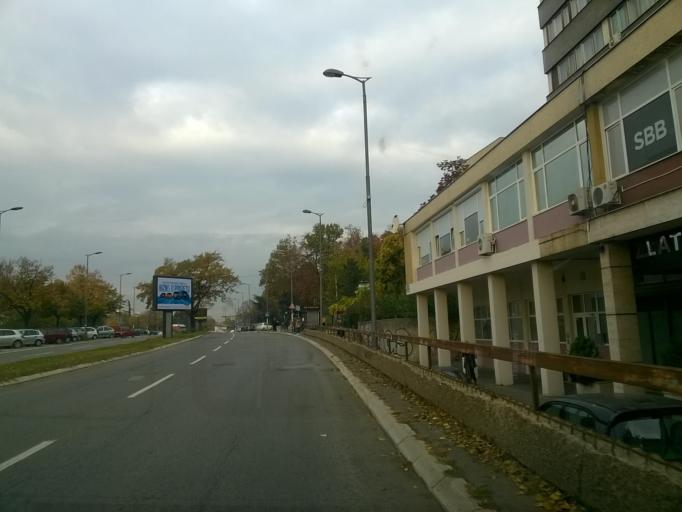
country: RS
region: Central Serbia
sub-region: Belgrade
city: Vracar
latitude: 44.7870
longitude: 20.4788
